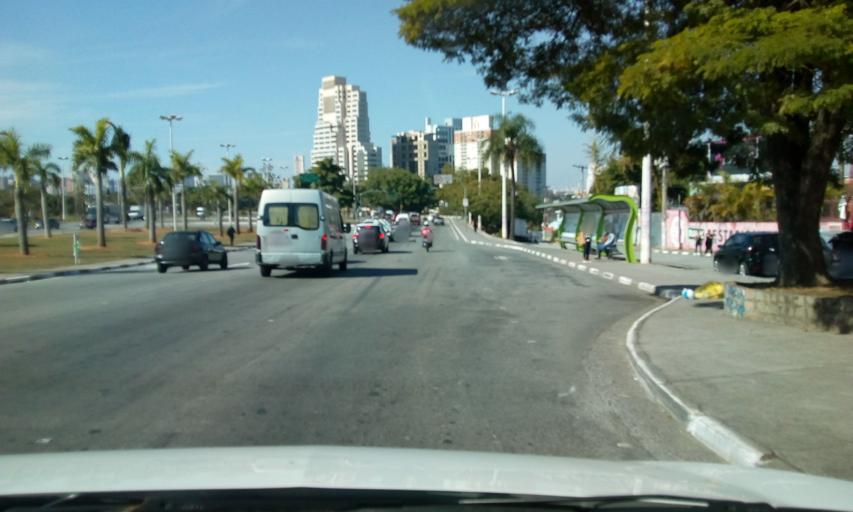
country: BR
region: Sao Paulo
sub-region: Barueri
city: Barueri
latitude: -23.5060
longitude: -46.8750
